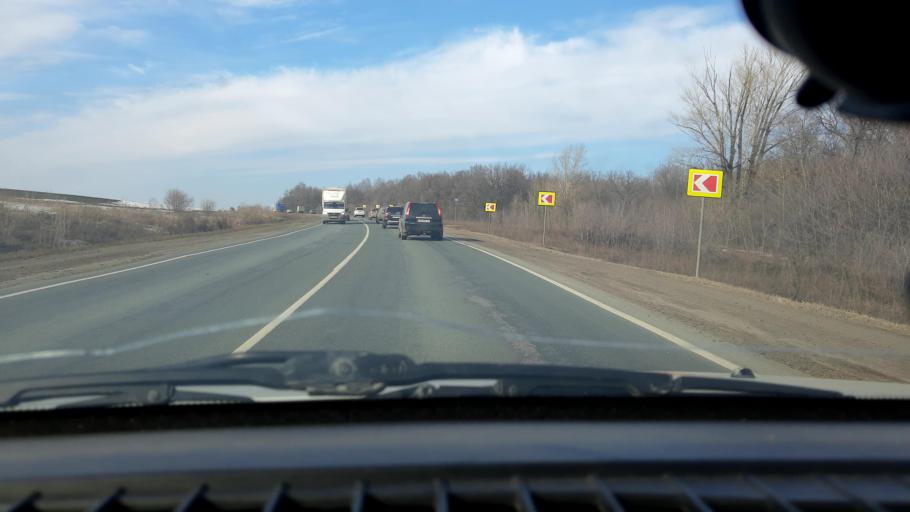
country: RU
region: Bashkortostan
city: Avdon
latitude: 54.7354
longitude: 55.7836
